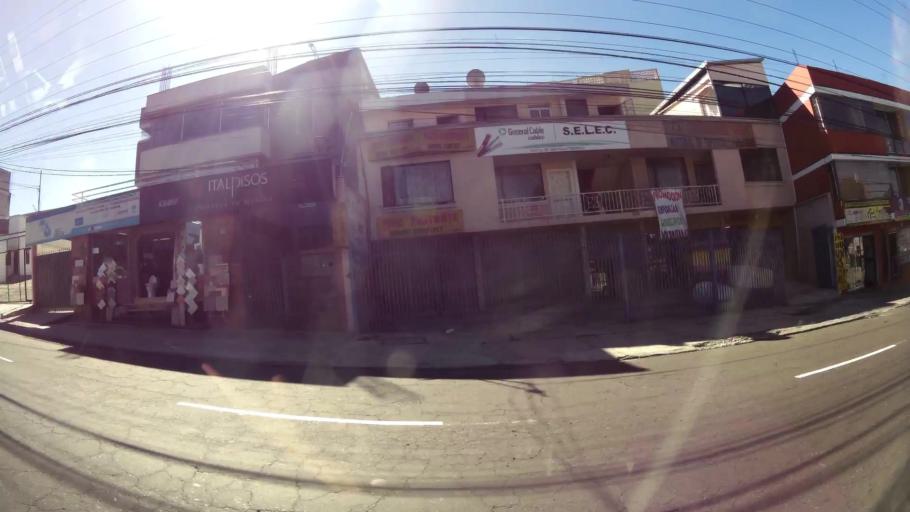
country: EC
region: Pichincha
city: Quito
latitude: -0.1377
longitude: -78.4734
